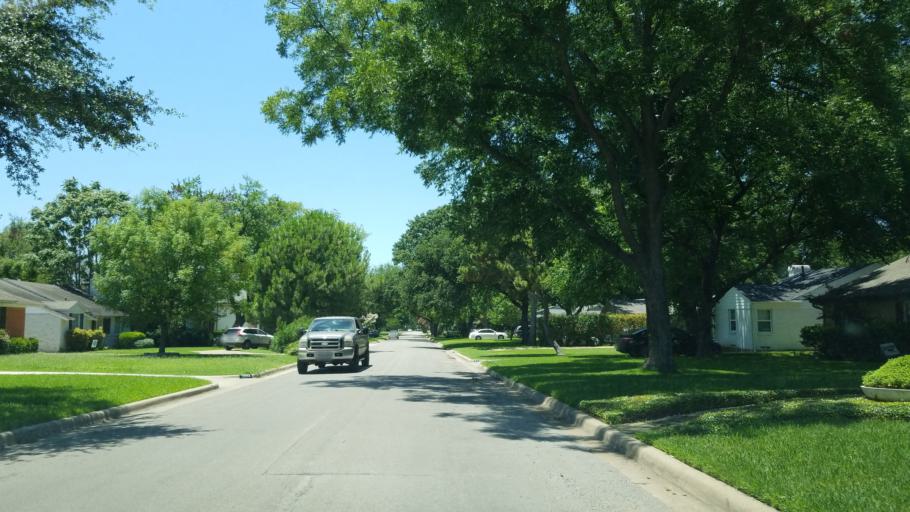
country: US
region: Texas
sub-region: Dallas County
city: University Park
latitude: 32.8716
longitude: -96.8493
